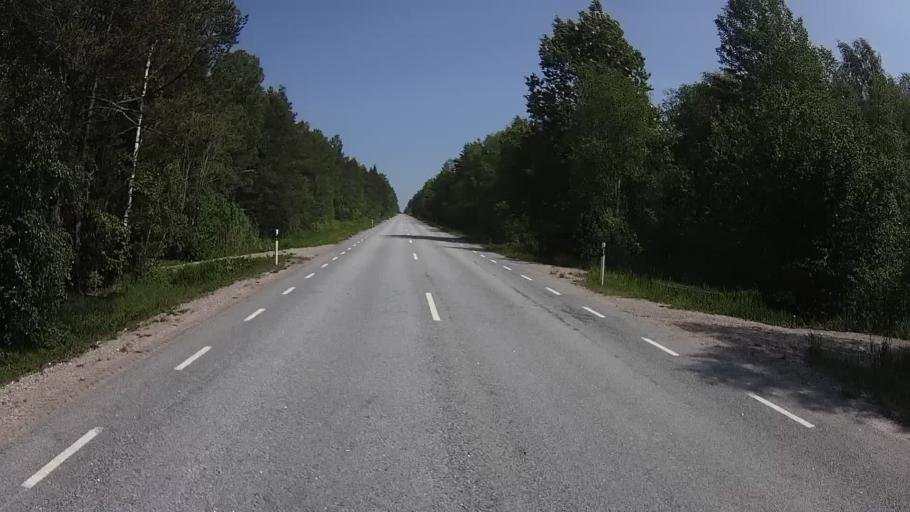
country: EE
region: Saare
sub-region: Kuressaare linn
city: Kuressaare
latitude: 58.3399
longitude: 22.1722
